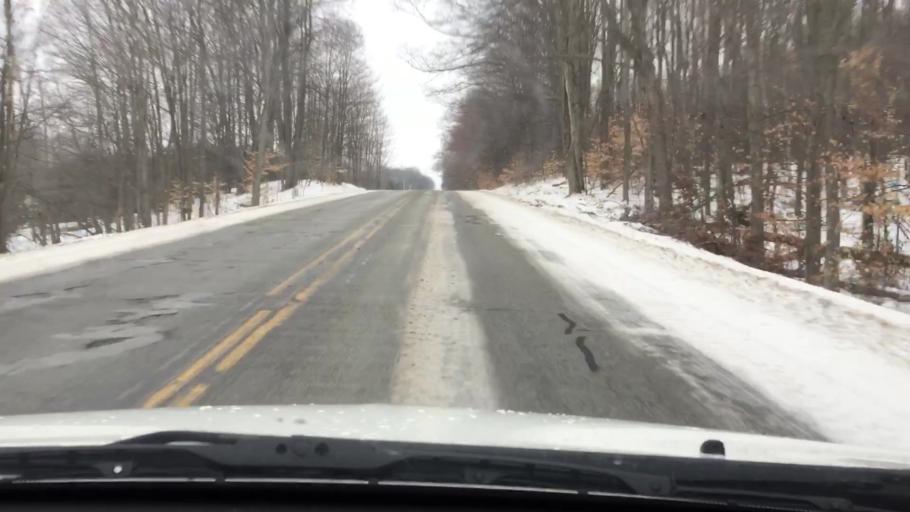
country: US
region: Michigan
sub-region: Wexford County
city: Cadillac
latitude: 44.1831
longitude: -85.4055
